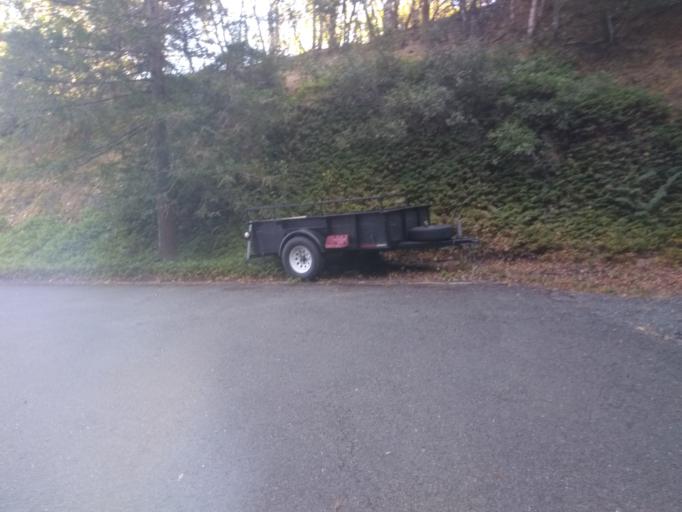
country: US
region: California
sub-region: Mendocino County
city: Ukiah
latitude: 39.1383
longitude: -123.2175
